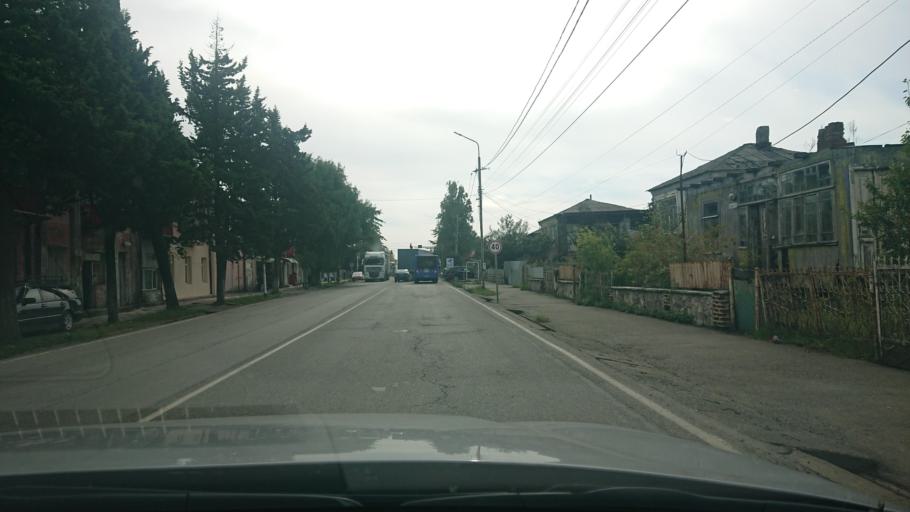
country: GE
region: Samegrelo and Zemo Svaneti
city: P'ot'i
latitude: 42.1570
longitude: 41.6693
